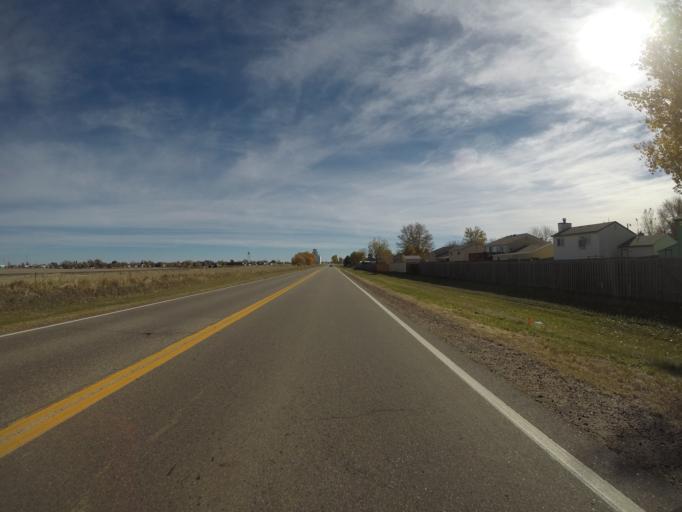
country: US
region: Colorado
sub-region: Adams County
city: Bennett
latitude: 39.7560
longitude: -104.4392
